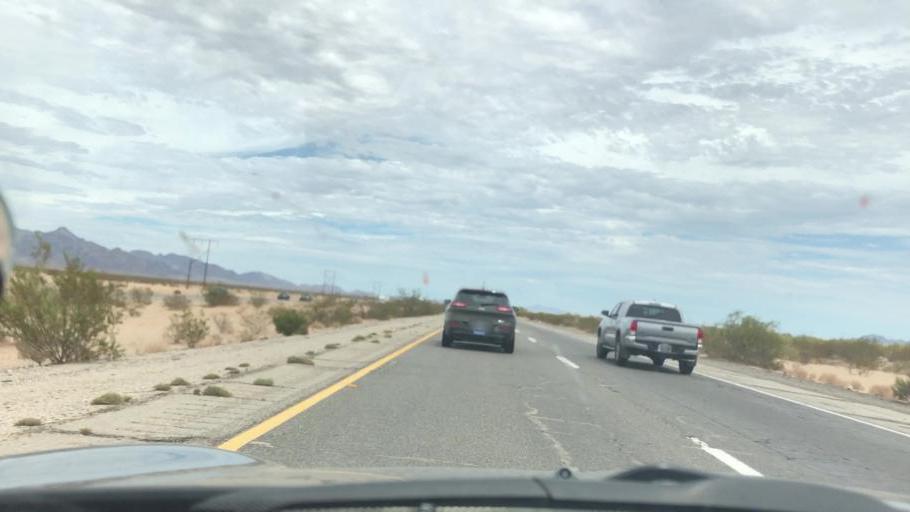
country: US
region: California
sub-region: Riverside County
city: Mesa Verde
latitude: 33.6059
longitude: -114.9589
